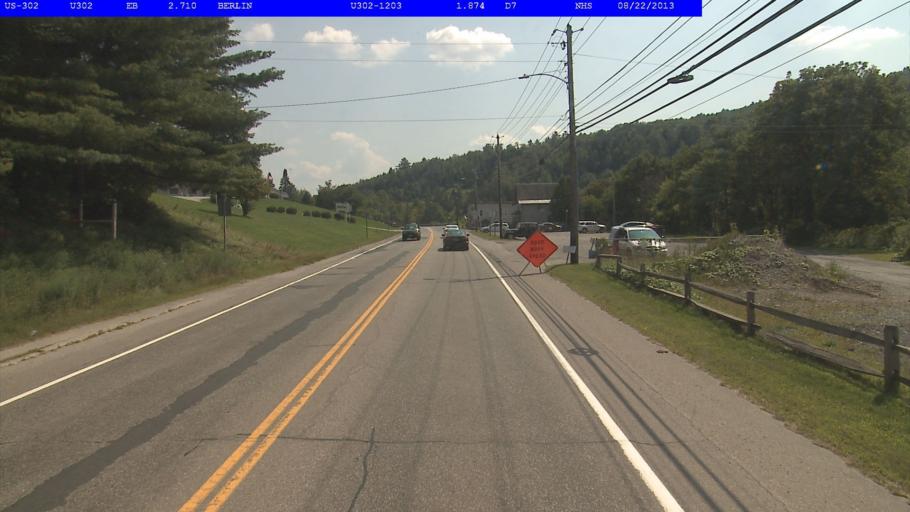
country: US
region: Vermont
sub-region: Washington County
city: Barre
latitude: 44.2149
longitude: -72.5346
